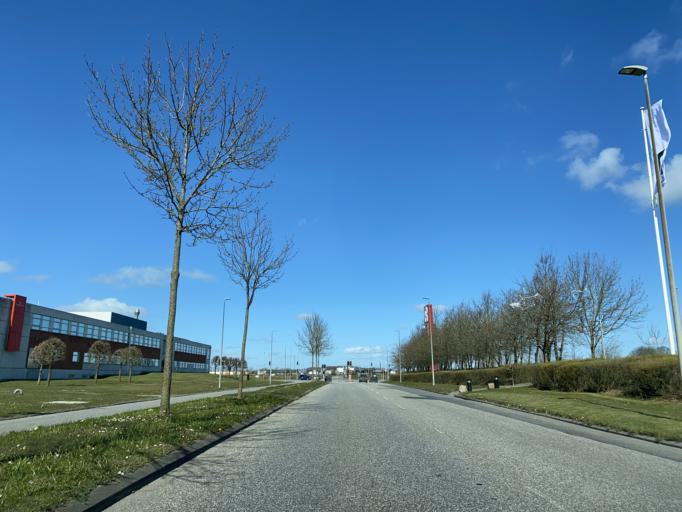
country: DK
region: Central Jutland
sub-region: Randers Kommune
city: Randers
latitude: 56.4291
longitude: 10.0615
